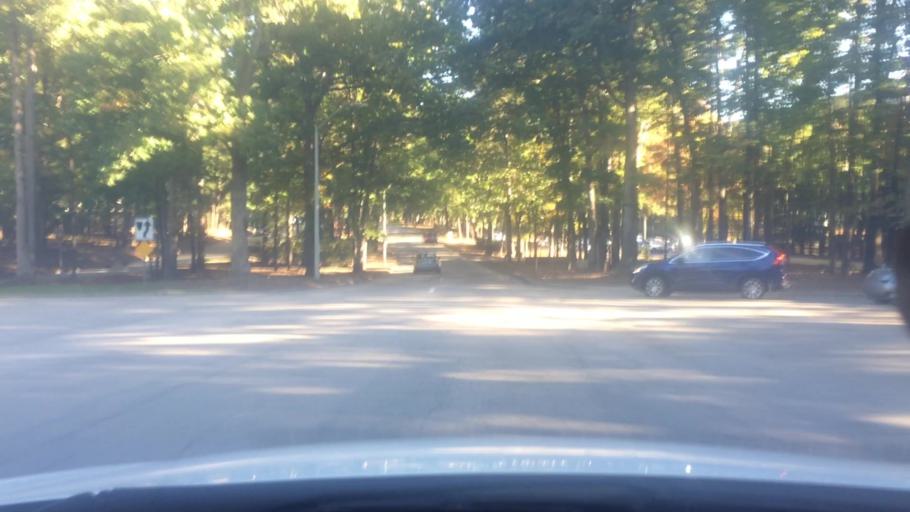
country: US
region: North Carolina
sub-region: Wake County
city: Raleigh
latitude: 35.8209
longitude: -78.6058
